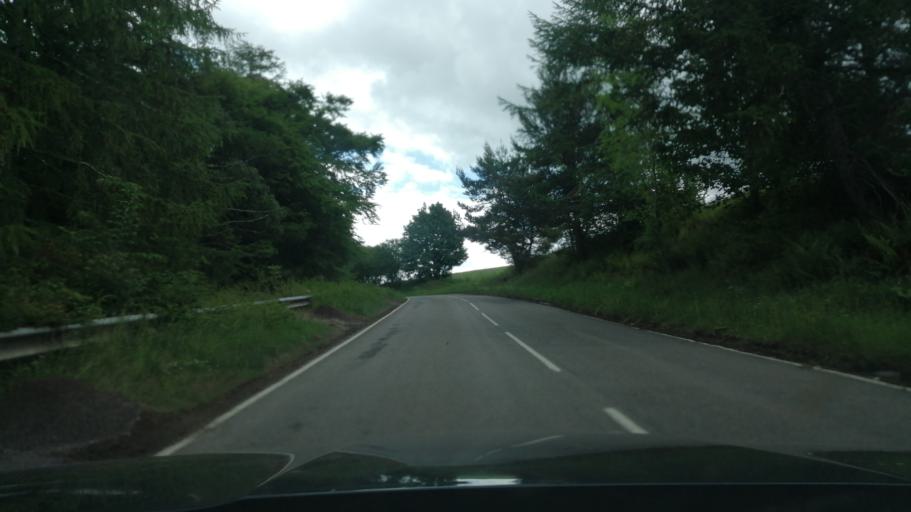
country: GB
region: Scotland
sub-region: Moray
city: Fochabers
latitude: 57.5493
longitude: -3.1325
